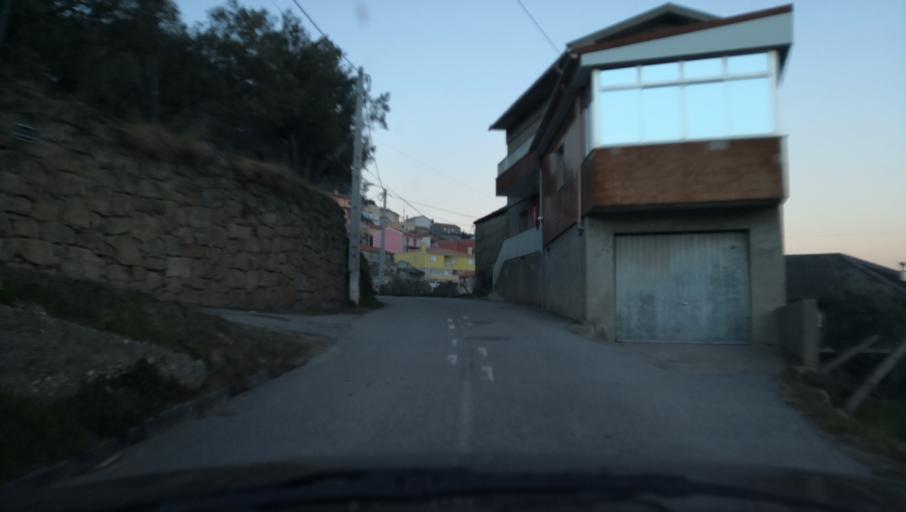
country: PT
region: Vila Real
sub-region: Vila Real
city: Vila Real
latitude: 41.3196
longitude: -7.7851
